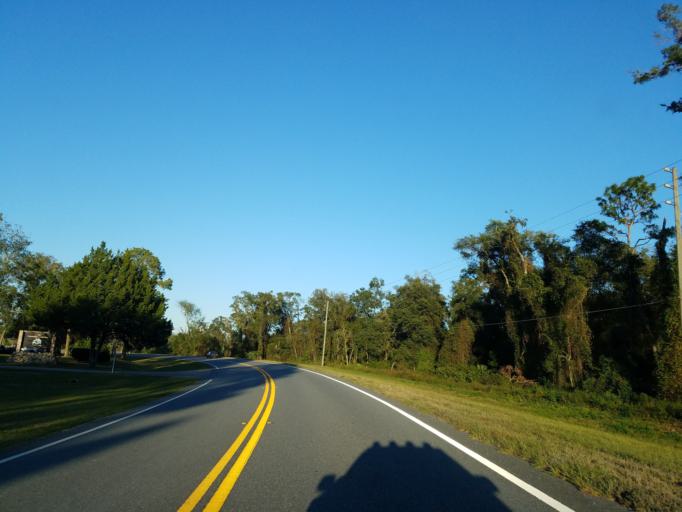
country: US
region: Florida
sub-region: Sumter County
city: Bushnell
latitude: 28.6125
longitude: -82.2049
